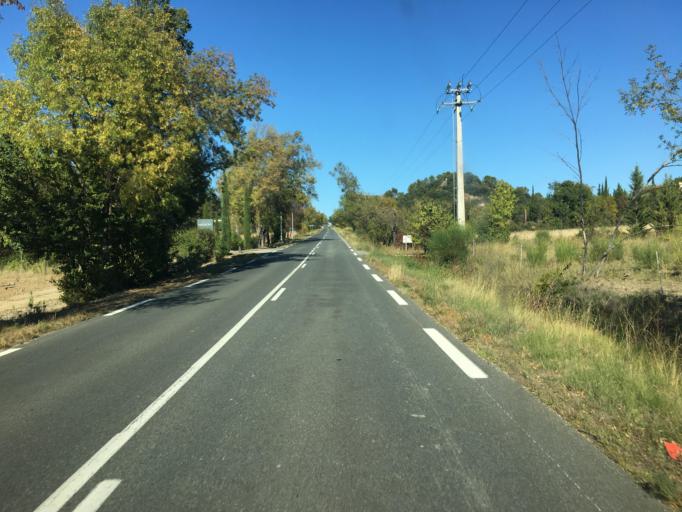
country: FR
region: Languedoc-Roussillon
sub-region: Departement de l'Herault
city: Nebian
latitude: 43.6144
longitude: 3.4079
